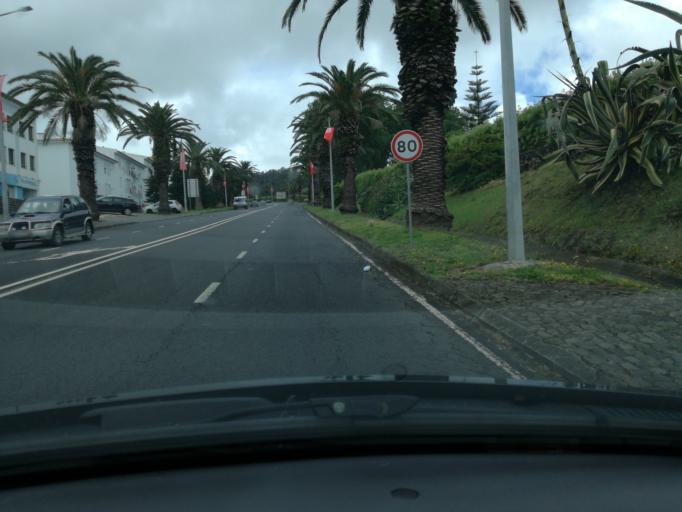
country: PT
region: Azores
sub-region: Angra do Heroismo
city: Angra do Heroismo
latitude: 38.6591
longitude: -27.2065
